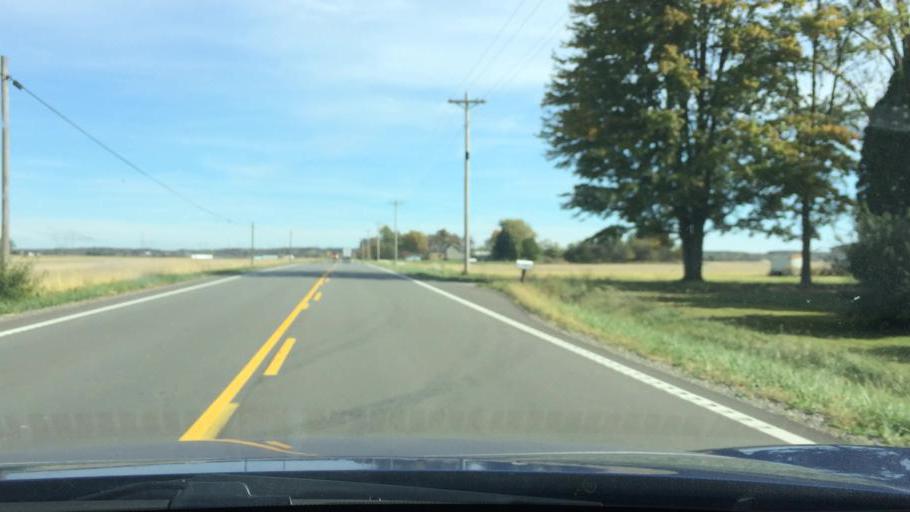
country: US
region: Ohio
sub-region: Logan County
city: Russells Point
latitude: 40.4449
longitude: -83.8301
